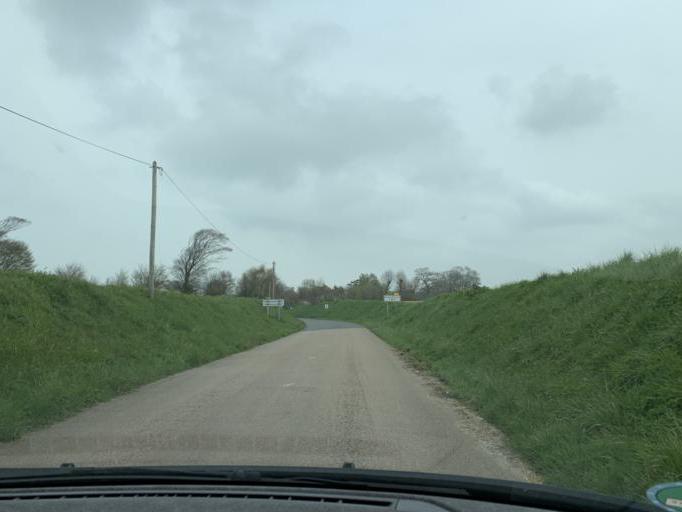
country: FR
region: Haute-Normandie
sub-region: Departement de la Seine-Maritime
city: Saint-Valery-en-Caux
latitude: 49.8538
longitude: 0.7852
